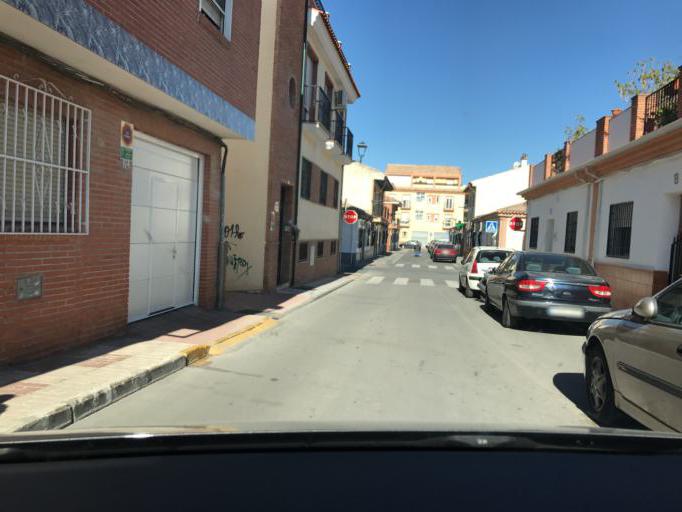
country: ES
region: Andalusia
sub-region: Provincia de Granada
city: Maracena
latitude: 37.2032
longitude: -3.6353
